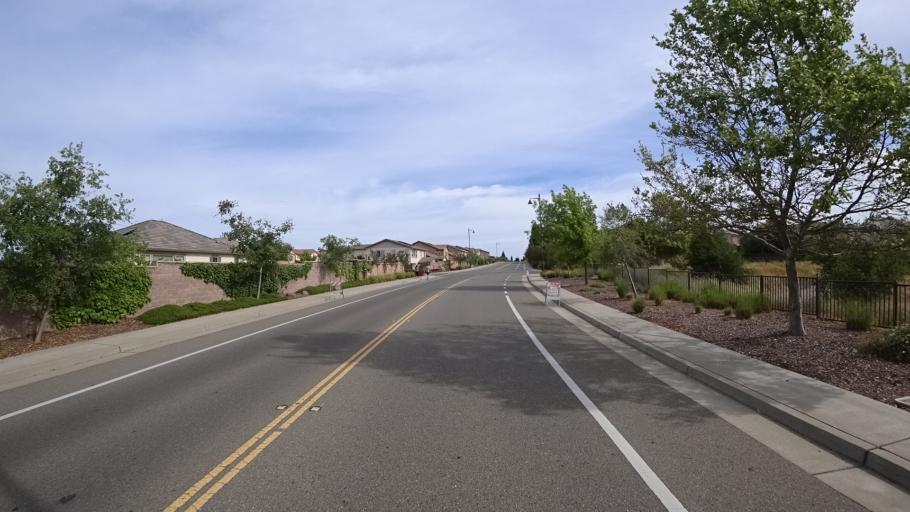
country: US
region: California
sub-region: Placer County
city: Lincoln
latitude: 38.8346
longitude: -121.2807
